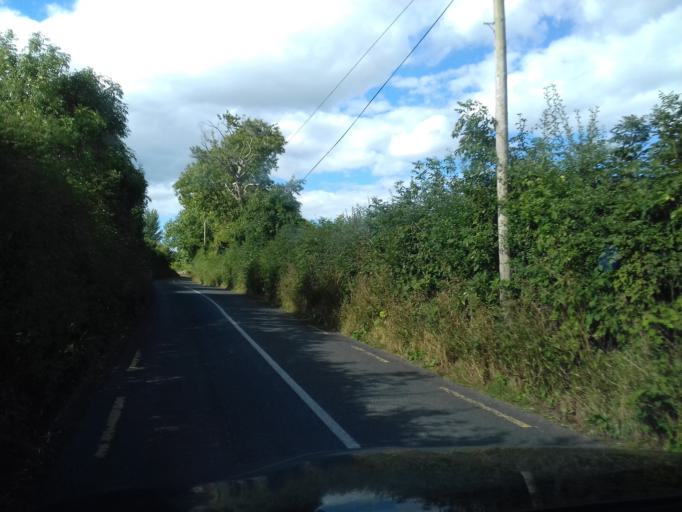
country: IE
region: Leinster
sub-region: Kilkenny
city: Thomastown
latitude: 52.5379
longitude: -7.0890
